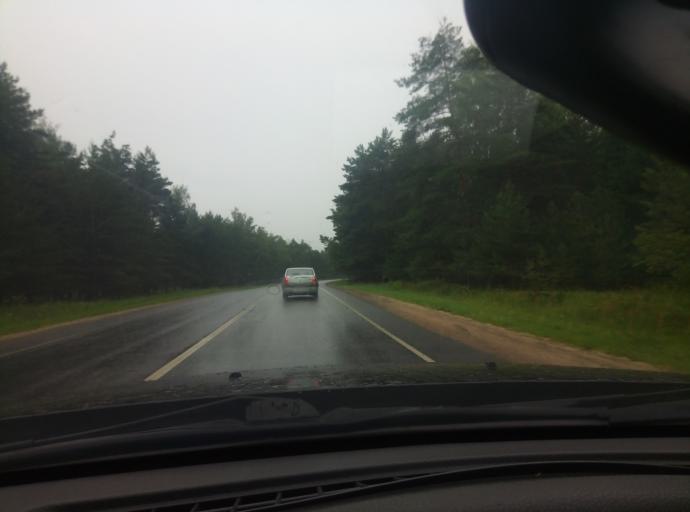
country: RU
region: Moskovskaya
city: Protvino
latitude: 54.8782
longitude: 37.2553
